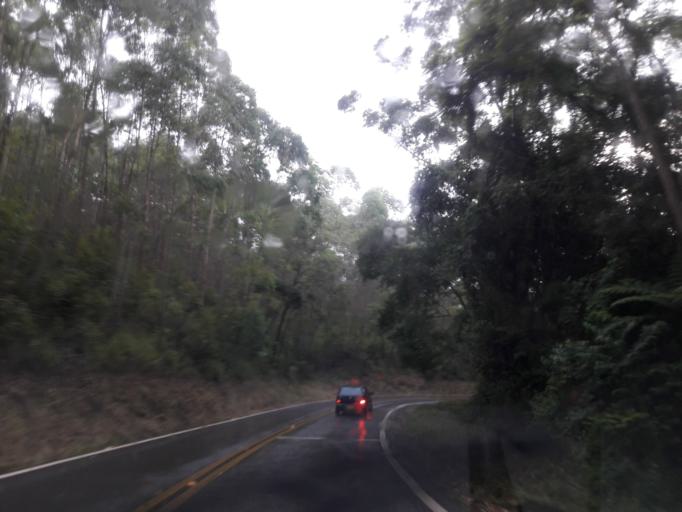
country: BR
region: Sao Paulo
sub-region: Aruja
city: Aruja
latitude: -23.2998
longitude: -46.4297
